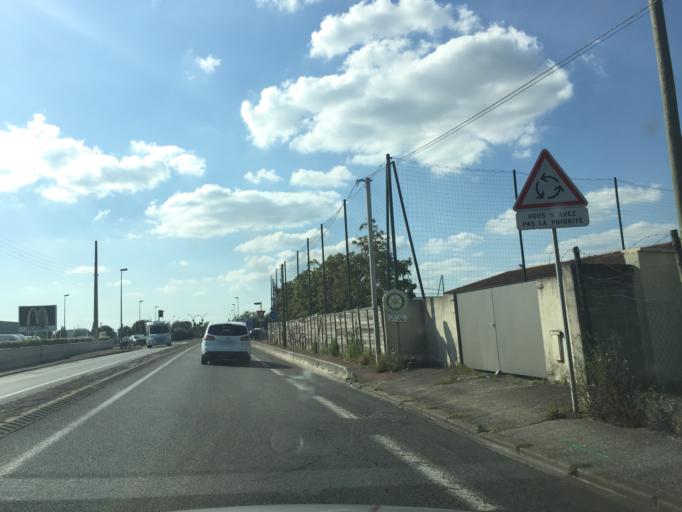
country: FR
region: Aquitaine
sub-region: Departement de la Gironde
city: Libourne
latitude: 44.8987
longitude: -0.2114
